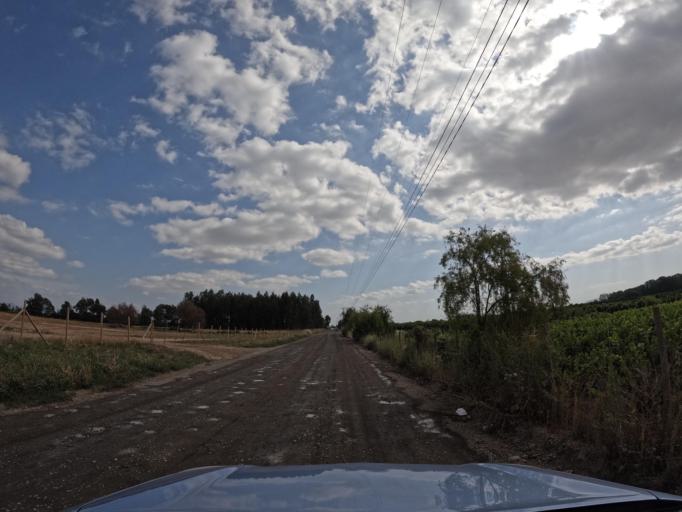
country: CL
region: Maule
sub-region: Provincia de Curico
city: Molina
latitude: -35.1654
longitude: -71.2895
